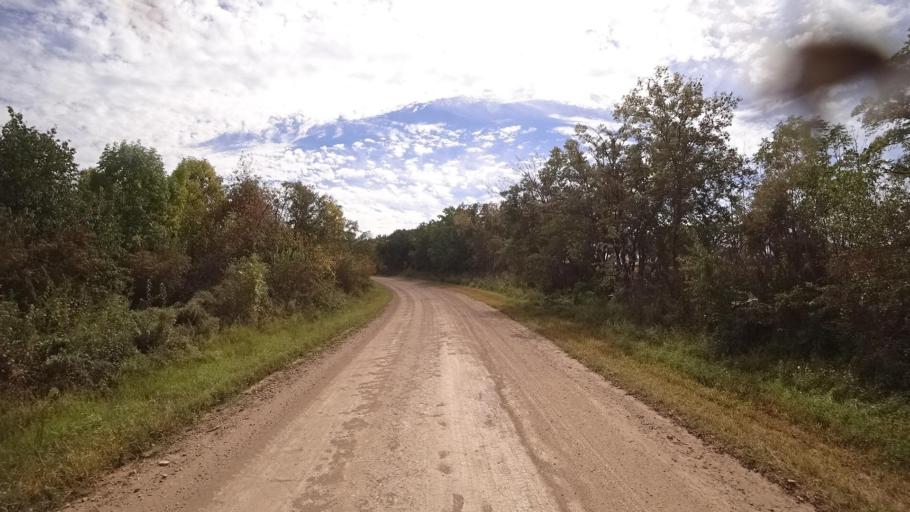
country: RU
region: Primorskiy
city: Yakovlevka
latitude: 44.5238
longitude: 133.5945
